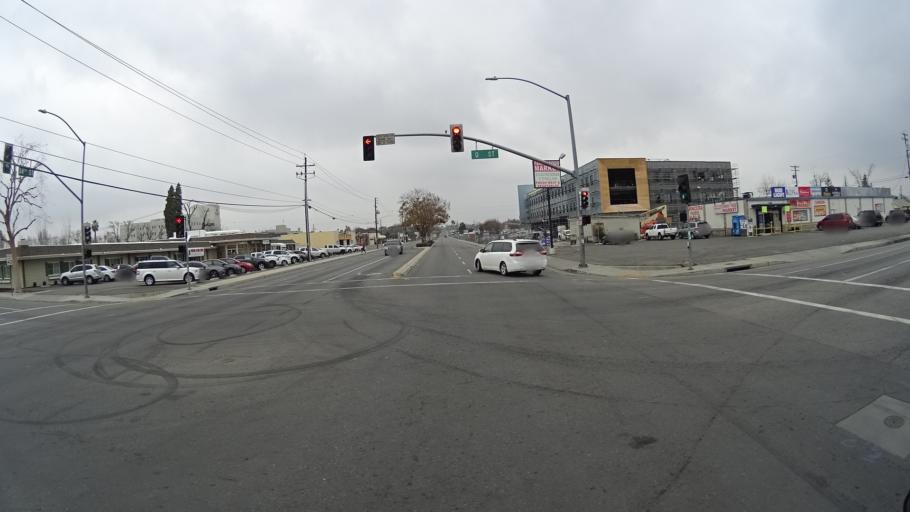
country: US
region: California
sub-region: Kern County
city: Bakersfield
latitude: 35.3905
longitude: -119.0107
